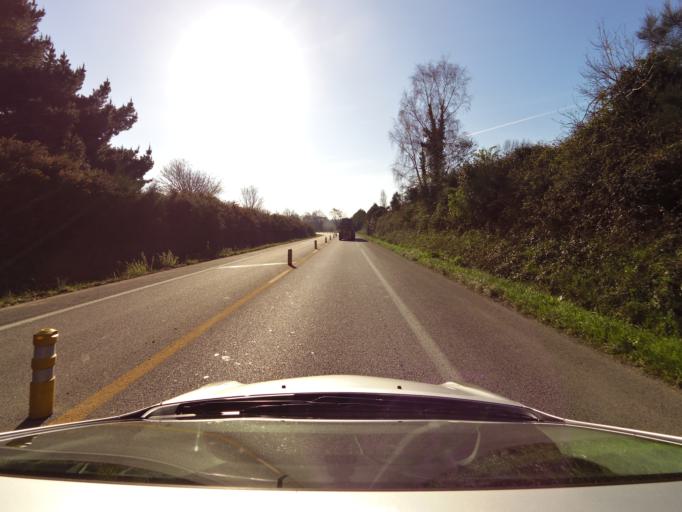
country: FR
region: Brittany
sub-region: Departement du Morbihan
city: Kervignac
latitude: 47.7878
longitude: -3.2488
